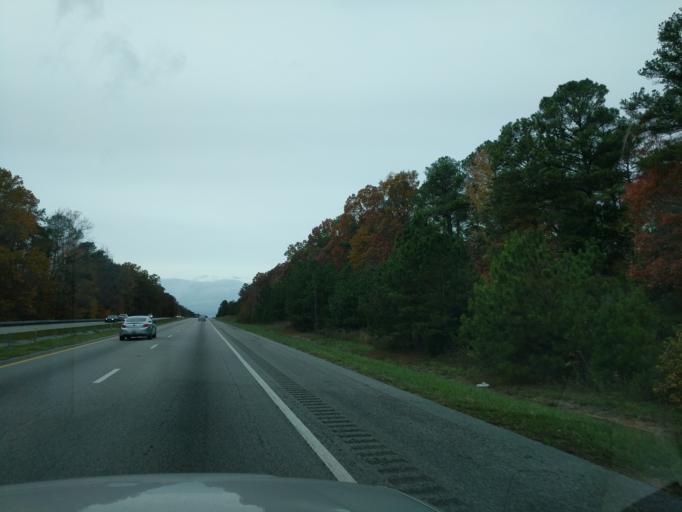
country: US
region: South Carolina
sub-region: Laurens County
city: Joanna
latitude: 34.4597
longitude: -81.7935
